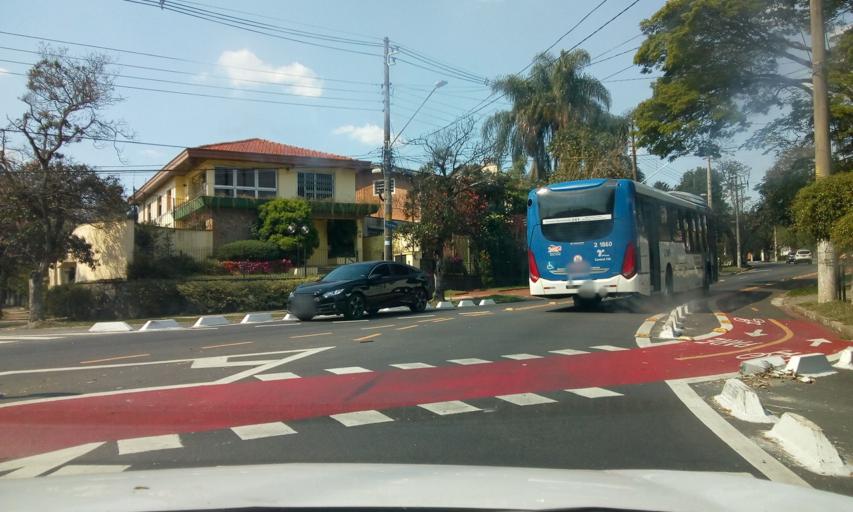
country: BR
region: Sao Paulo
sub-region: Osasco
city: Osasco
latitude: -23.5250
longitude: -46.7234
